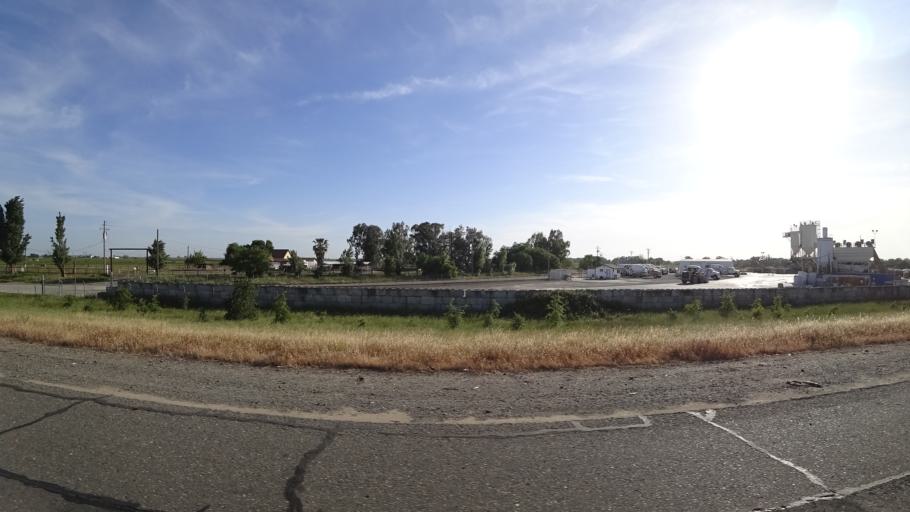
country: US
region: California
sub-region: Yuba County
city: Olivehurst
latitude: 39.0691
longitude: -121.5202
